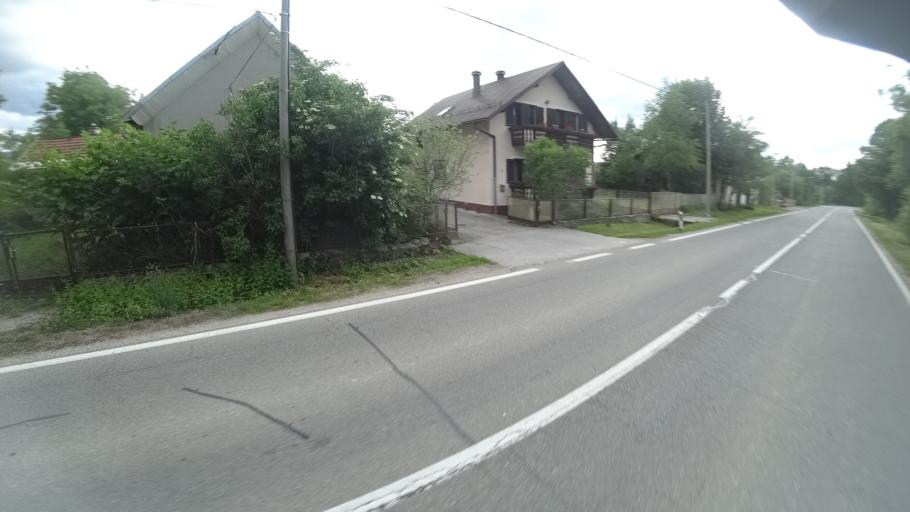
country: HR
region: Licko-Senjska
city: Gospic
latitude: 44.5158
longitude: 15.4200
